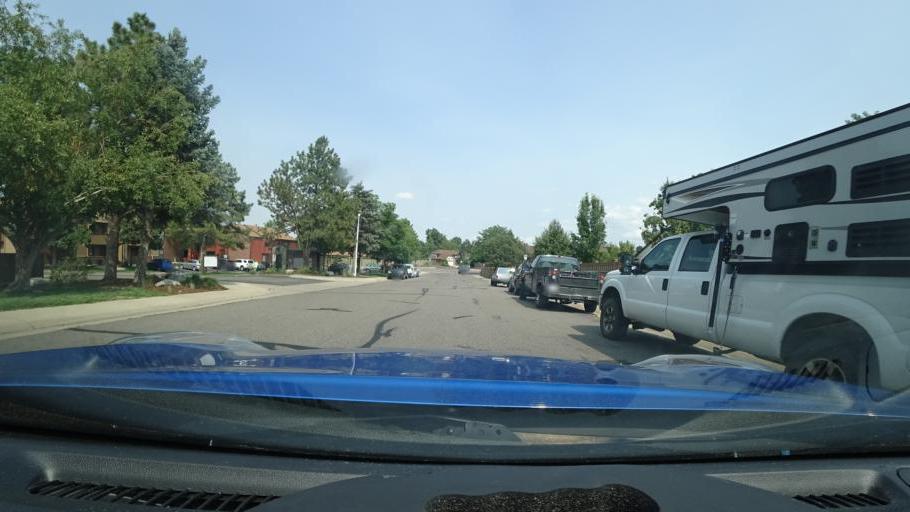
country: US
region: Colorado
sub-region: Adams County
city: Aurora
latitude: 39.6699
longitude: -104.8486
